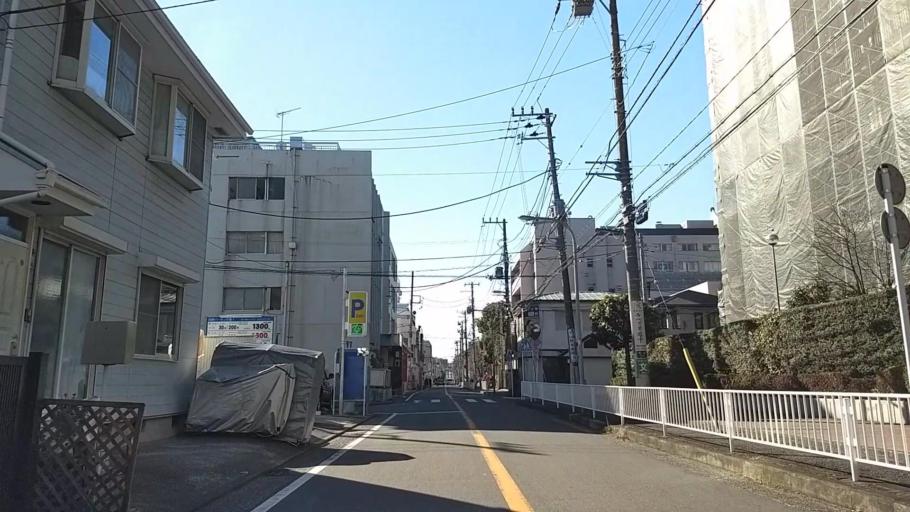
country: JP
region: Kanagawa
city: Yokohama
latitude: 35.4614
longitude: 139.6157
